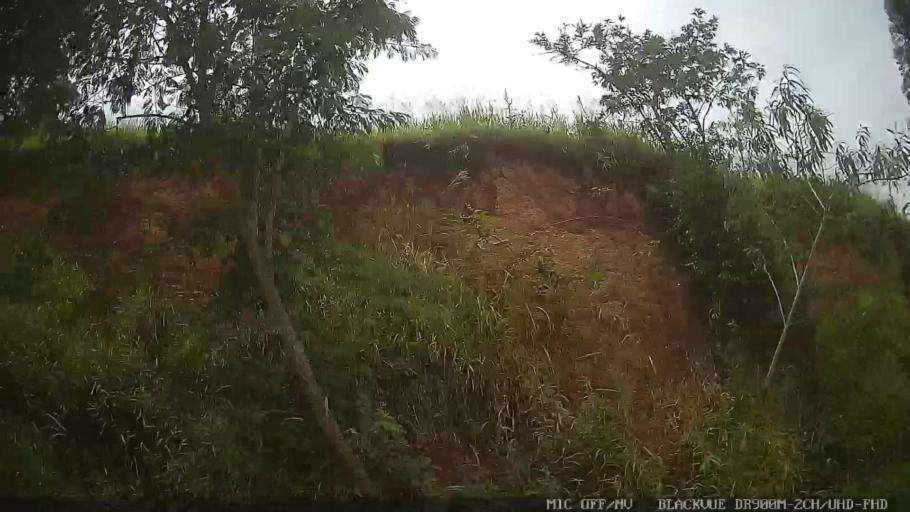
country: BR
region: Sao Paulo
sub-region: Santa Isabel
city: Santa Isabel
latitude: -23.3362
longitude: -46.2238
